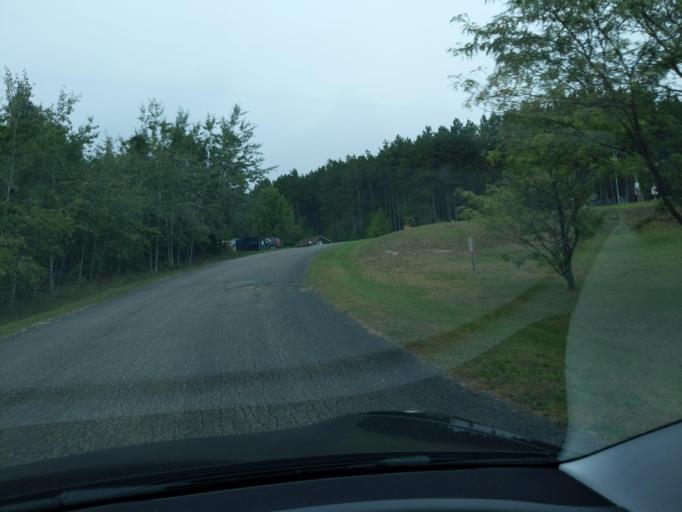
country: US
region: Michigan
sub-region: Antrim County
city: Elk Rapids
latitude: 44.8156
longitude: -85.3874
